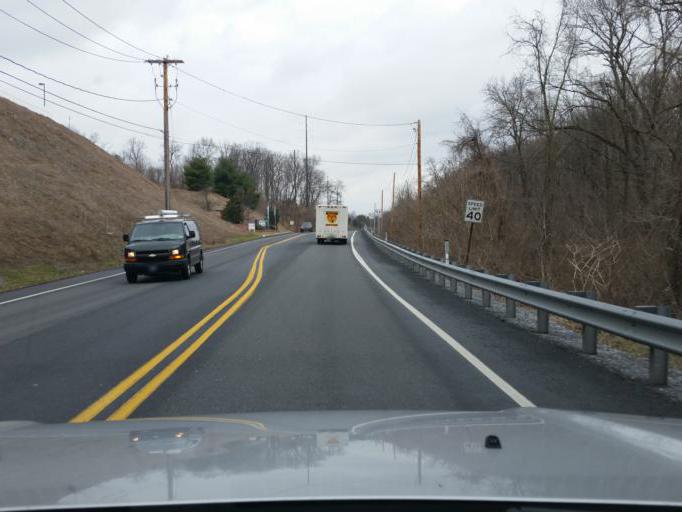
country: US
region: Pennsylvania
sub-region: Dauphin County
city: Rutherford
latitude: 40.2990
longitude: -76.7671
